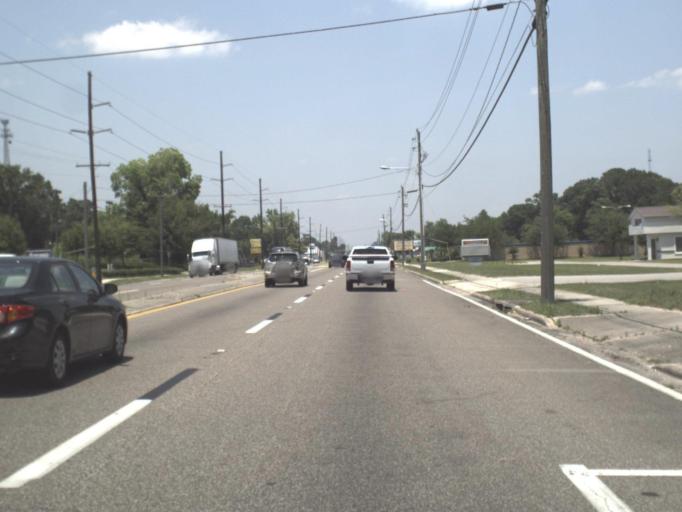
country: US
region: Florida
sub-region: Bradford County
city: Starke
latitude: 29.9604
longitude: -82.1056
